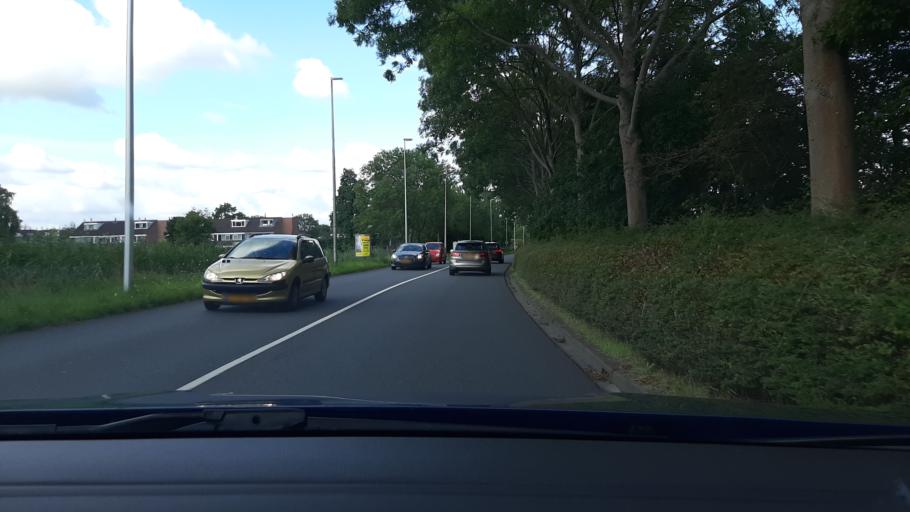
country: NL
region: North Holland
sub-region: Gemeente Purmerend
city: Purmerend
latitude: 52.4977
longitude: 4.9558
